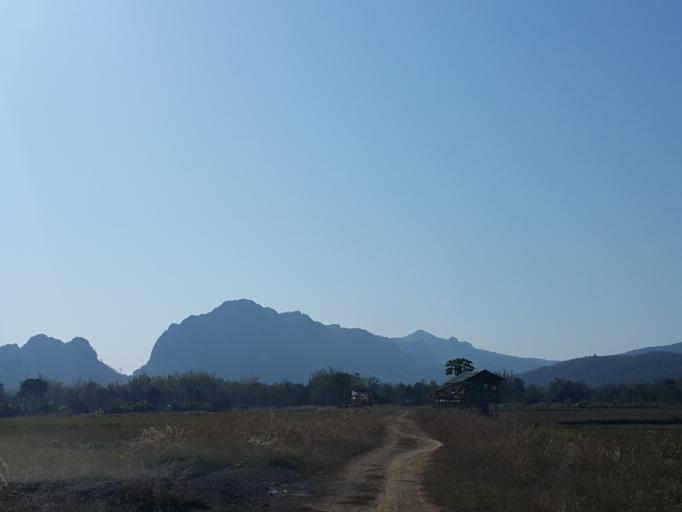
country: TH
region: Sukhothai
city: Thung Saliam
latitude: 17.3168
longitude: 99.4347
